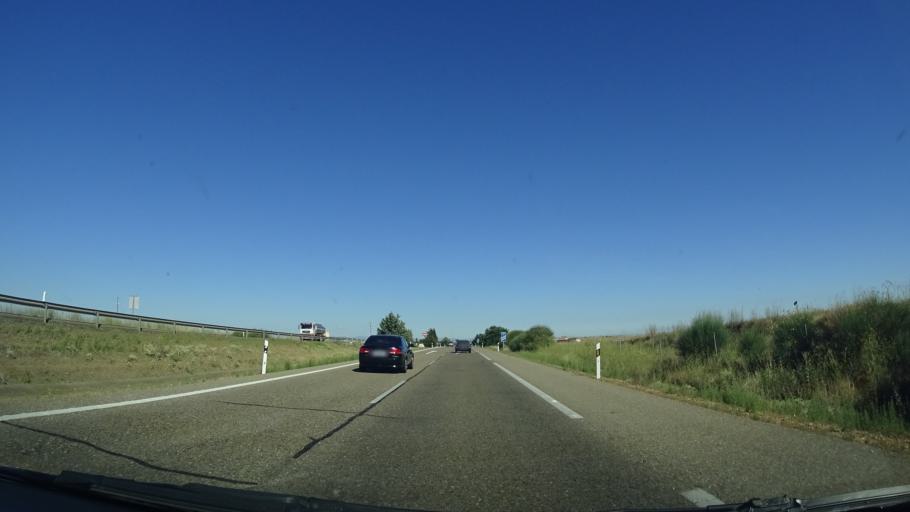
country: ES
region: Castille and Leon
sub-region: Provincia de Zamora
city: San Esteban del Molar
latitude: 41.9325
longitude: -5.5376
